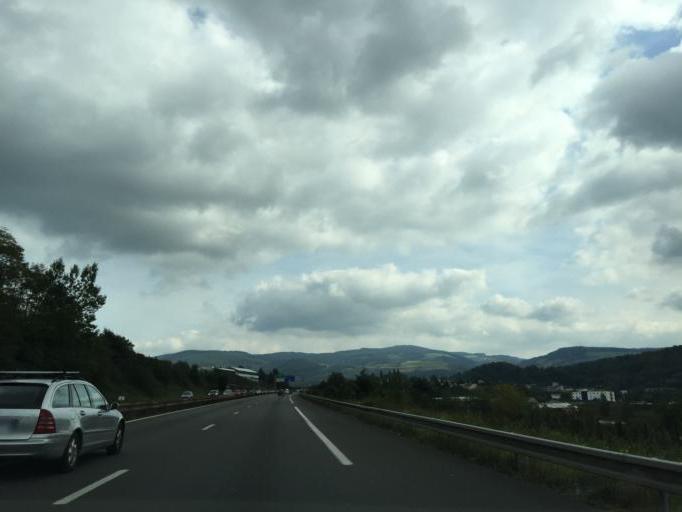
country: FR
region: Rhone-Alpes
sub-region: Departement de la Loire
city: Saint-Jean-Bonnefonds
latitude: 45.4490
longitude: 4.4222
